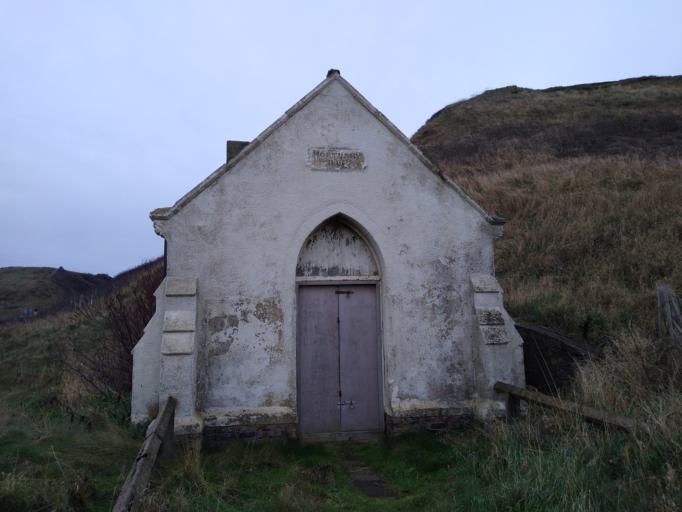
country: GB
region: England
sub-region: Redcar and Cleveland
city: Saltburn-by-the-Sea
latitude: 54.5851
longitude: -0.9657
